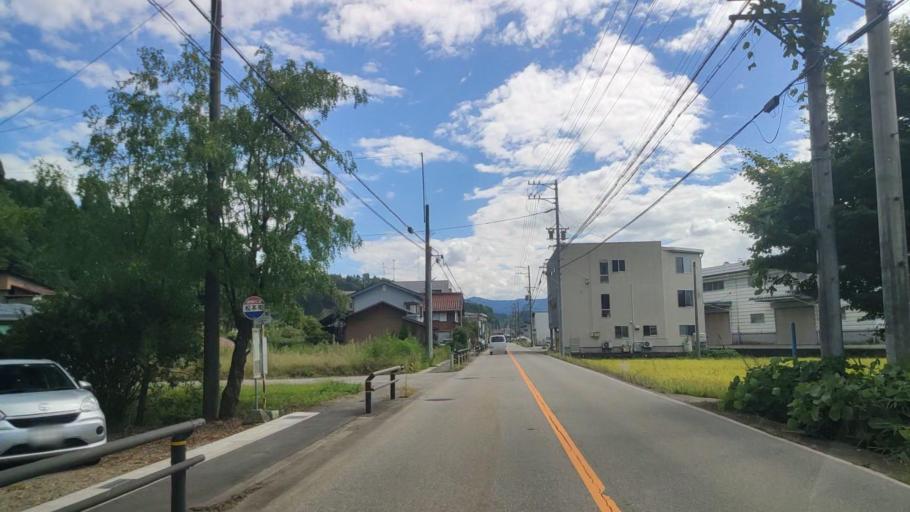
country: JP
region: Gifu
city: Takayama
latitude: 36.1650
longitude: 137.2500
